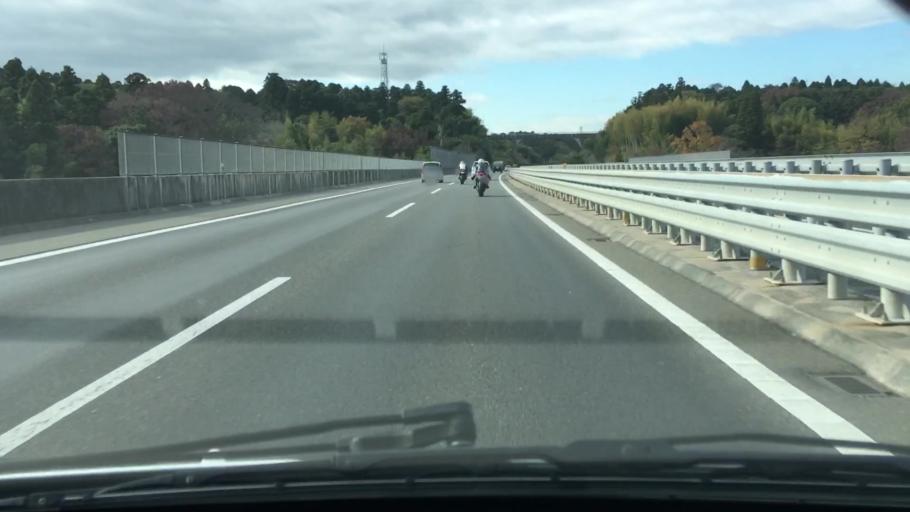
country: JP
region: Chiba
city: Ichihara
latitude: 35.4475
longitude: 140.0756
